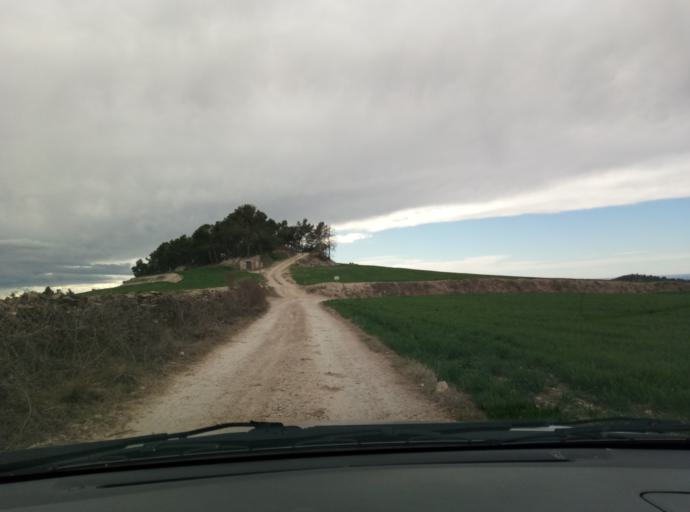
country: ES
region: Catalonia
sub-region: Provincia de Lleida
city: Nalec
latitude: 41.5151
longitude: 1.1441
